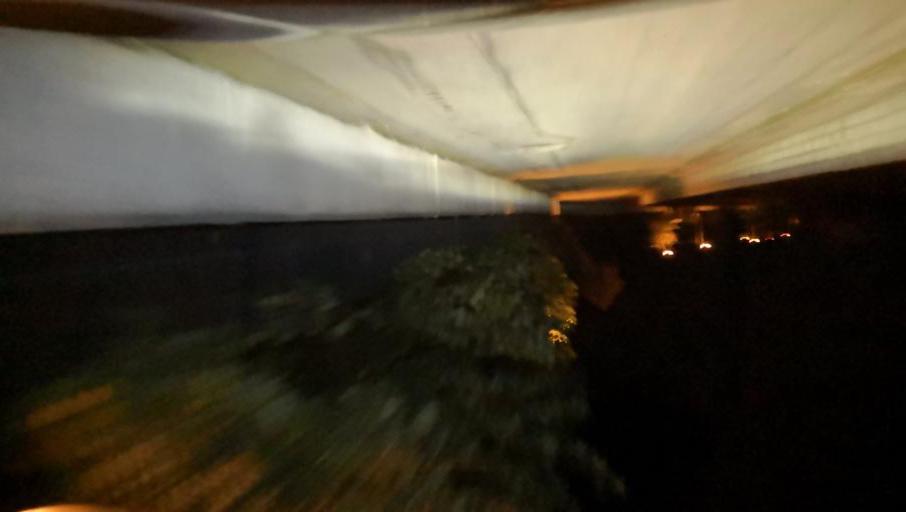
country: PT
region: Vila Real
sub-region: Peso da Regua
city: Peso da Regua
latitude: 41.1813
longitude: -7.7212
